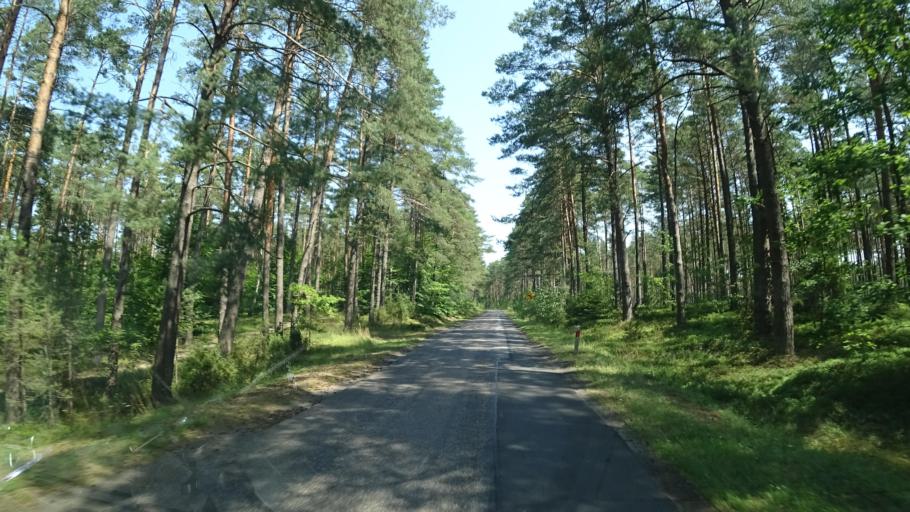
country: PL
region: Pomeranian Voivodeship
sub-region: Powiat chojnicki
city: Brusy
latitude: 53.8690
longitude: 17.6194
